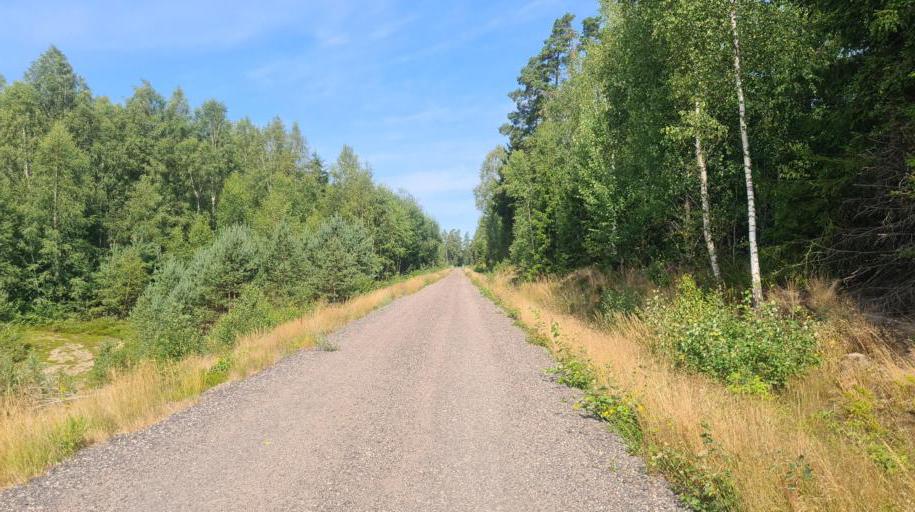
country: SE
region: Kronoberg
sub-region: Ljungby Kommun
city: Lagan
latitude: 56.9261
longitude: 13.9829
